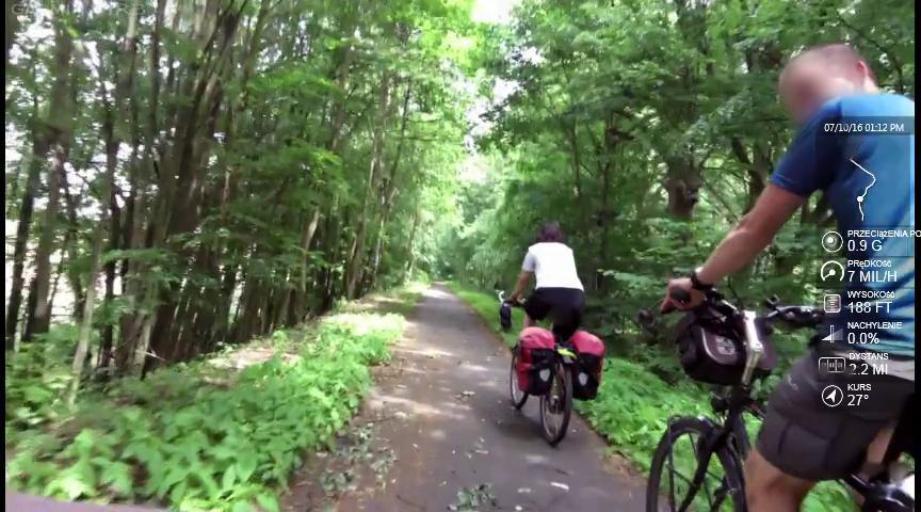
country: PL
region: West Pomeranian Voivodeship
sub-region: Powiat gryfinski
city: Banie
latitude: 53.0685
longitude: 14.6282
